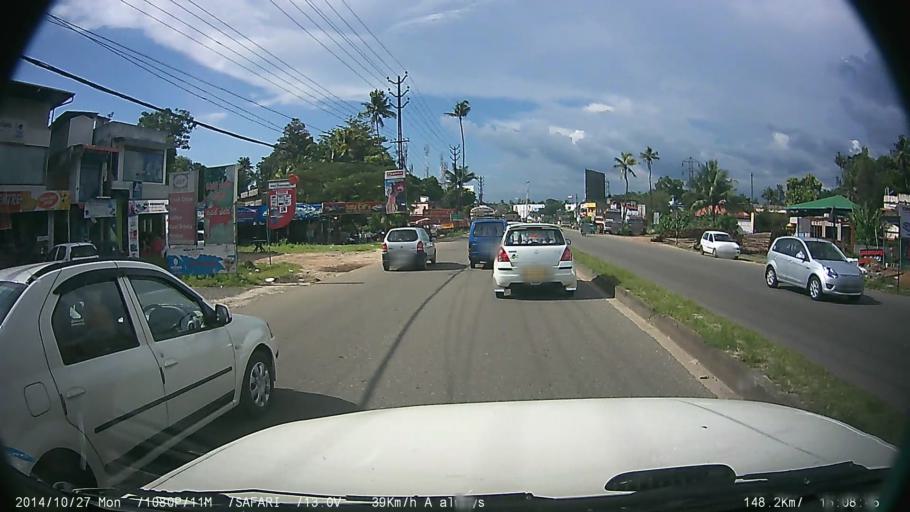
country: IN
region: Kerala
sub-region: Ernakulam
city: Aluva
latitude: 10.1168
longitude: 76.3445
